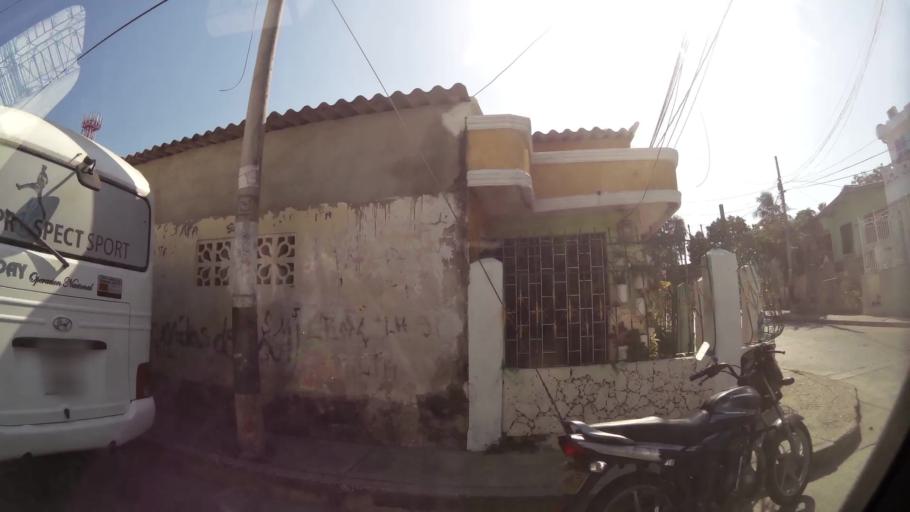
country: CO
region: Bolivar
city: Cartagena
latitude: 10.3994
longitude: -75.4986
